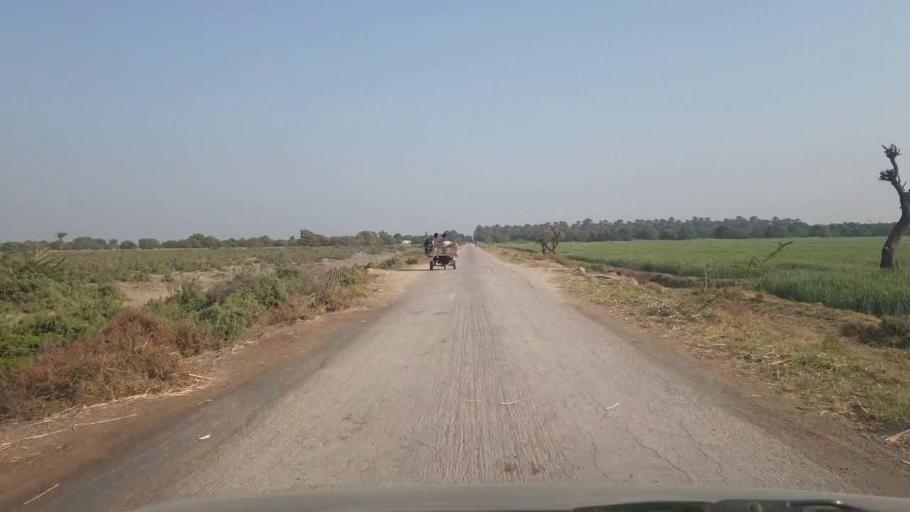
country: PK
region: Sindh
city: Digri
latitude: 25.2627
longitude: 69.1730
